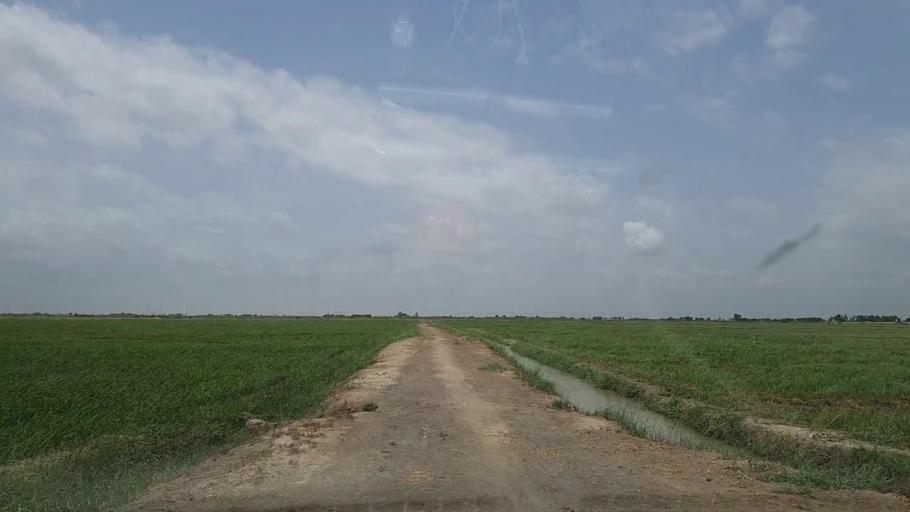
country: PK
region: Sindh
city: Thatta
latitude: 24.6233
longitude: 68.0414
